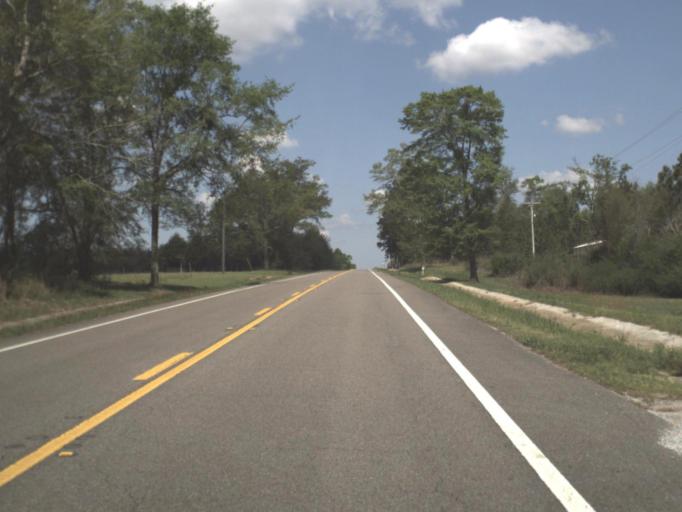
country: US
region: Alabama
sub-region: Escambia County
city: East Brewton
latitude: 30.9236
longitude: -87.0505
